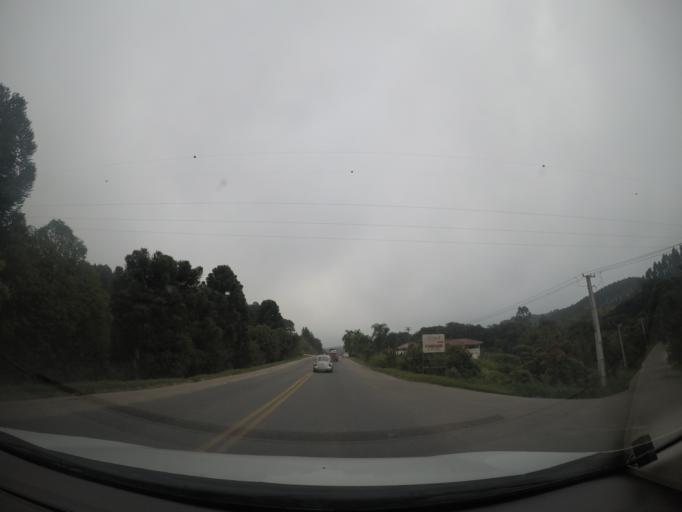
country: BR
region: Parana
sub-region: Almirante Tamandare
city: Almirante Tamandare
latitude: -25.3367
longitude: -49.2844
